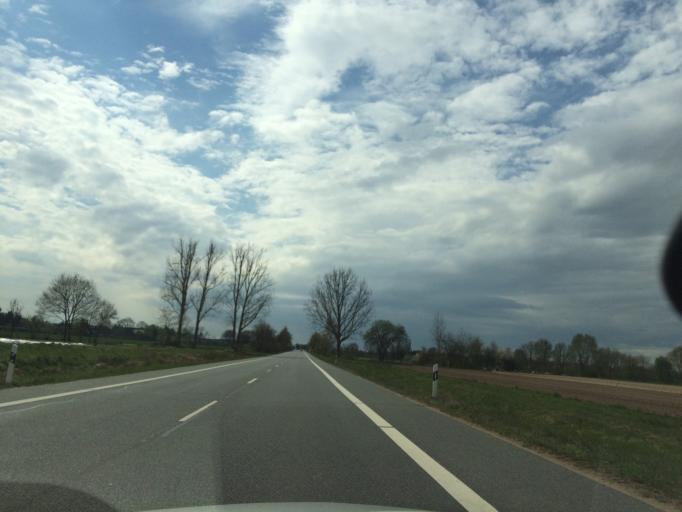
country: DE
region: Hesse
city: Weiterstadt
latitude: 49.9370
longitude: 8.5937
